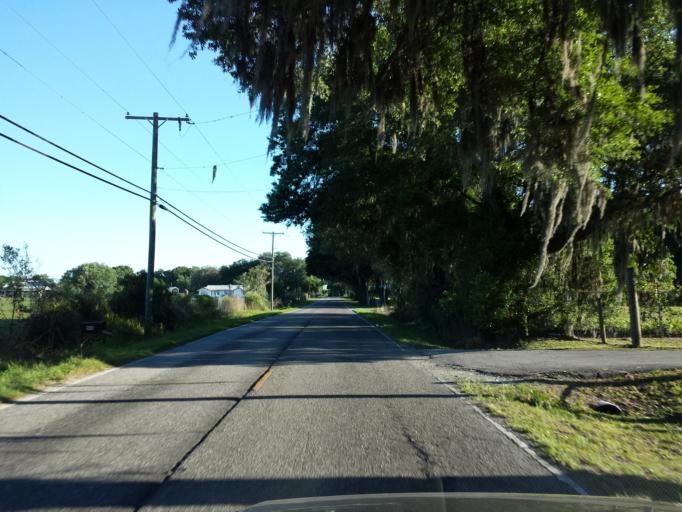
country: US
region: Florida
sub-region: Hillsborough County
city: Dover
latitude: 28.0386
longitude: -82.2491
